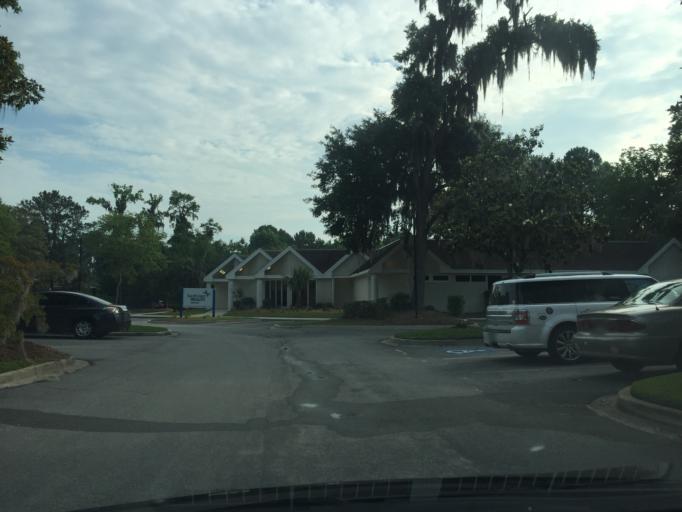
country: US
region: Georgia
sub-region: Chatham County
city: Isle of Hope
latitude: 32.0095
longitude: -81.1077
